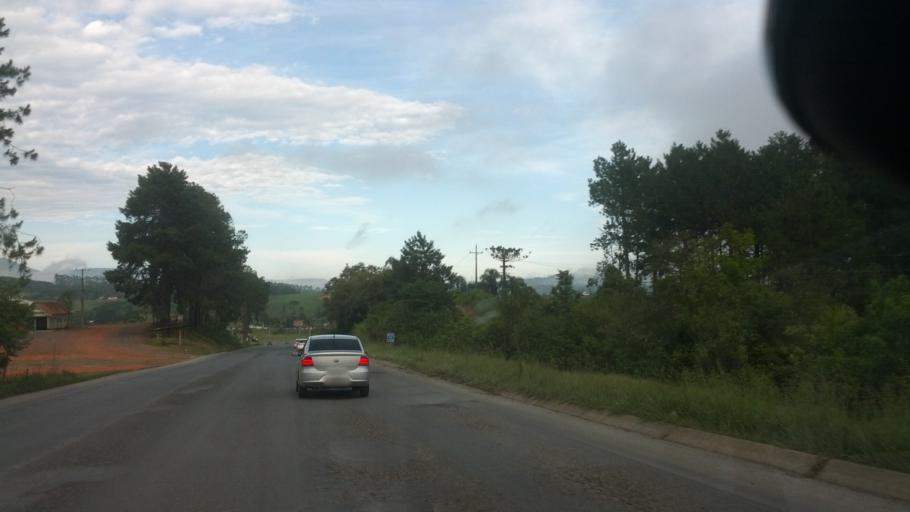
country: BR
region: Santa Catarina
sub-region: Otacilio Costa
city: Otacilio Costa
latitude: -27.2527
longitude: -49.9523
